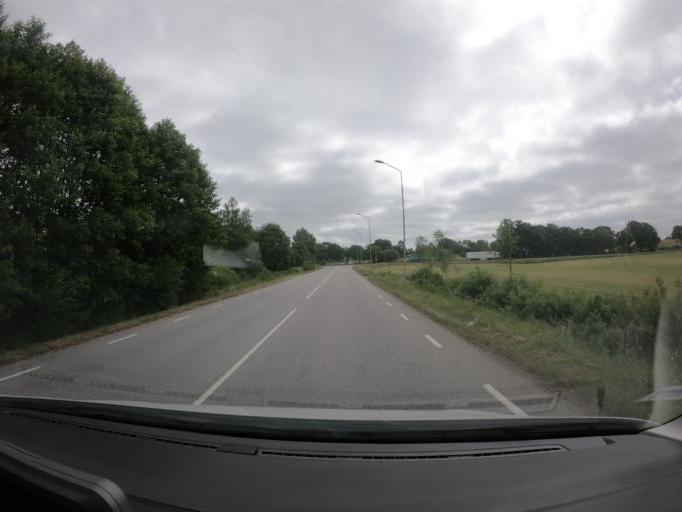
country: SE
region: Skane
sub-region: Hassleholms Kommun
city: Sosdala
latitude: 56.0067
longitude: 13.6491
